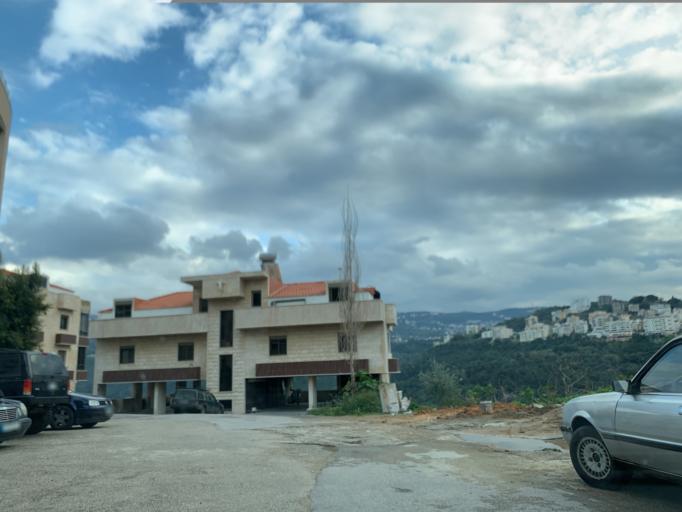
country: LB
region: Mont-Liban
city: Baabda
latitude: 33.8491
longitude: 35.5654
